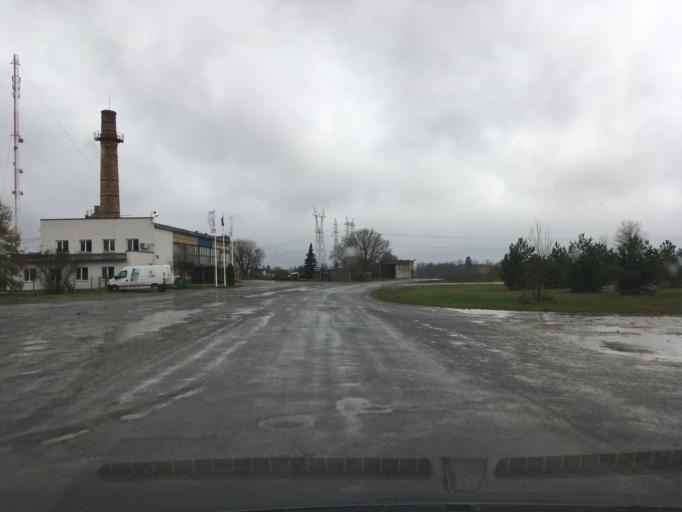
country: EE
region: Laeaene
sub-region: Lihula vald
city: Lihula
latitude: 58.6769
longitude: 23.8229
